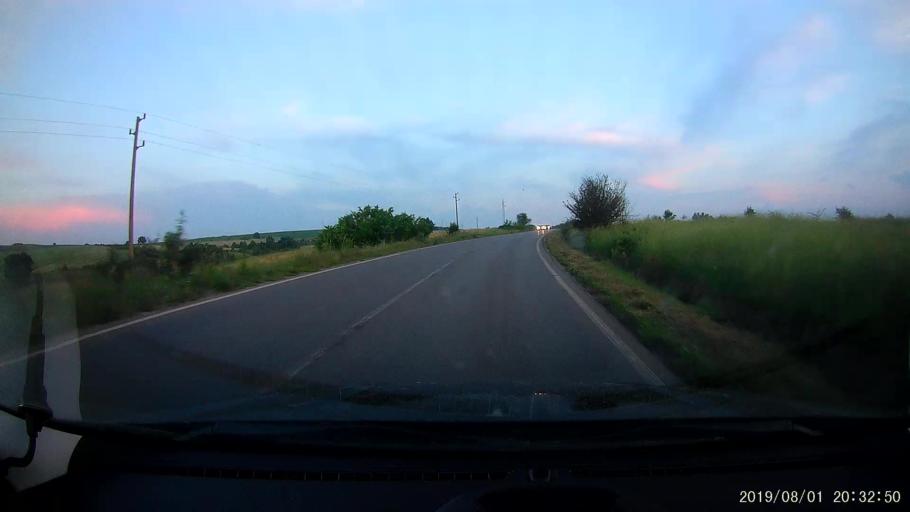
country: BG
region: Yambol
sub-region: Obshtina Elkhovo
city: Elkhovo
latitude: 42.1159
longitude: 26.5311
